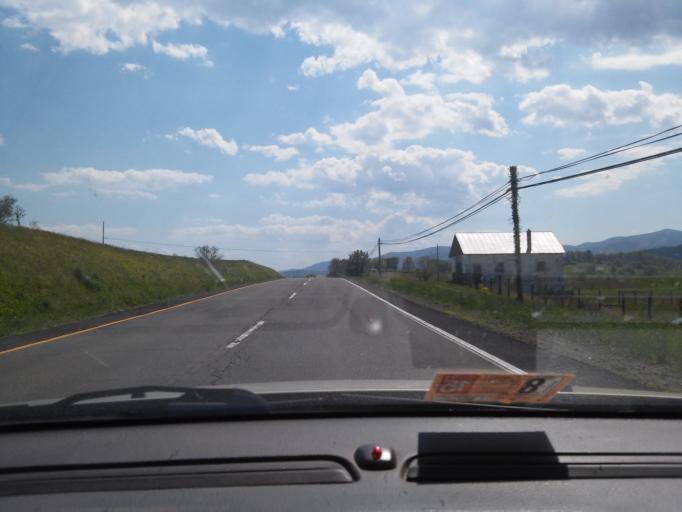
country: US
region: Virginia
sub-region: Rappahannock County
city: Washington
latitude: 38.6791
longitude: -78.2080
